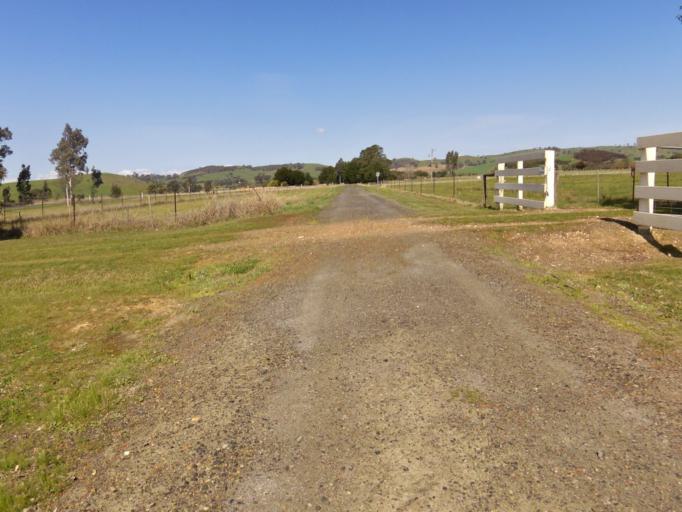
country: AU
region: Victoria
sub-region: Murrindindi
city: Alexandra
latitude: -37.0054
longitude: 145.7496
